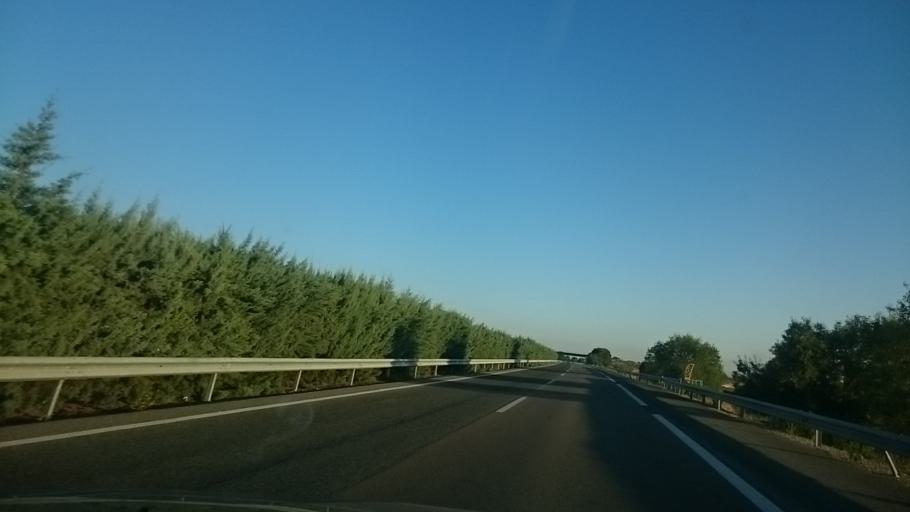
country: ES
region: Navarre
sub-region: Provincia de Navarra
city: Corella
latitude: 42.1103
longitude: -1.7322
